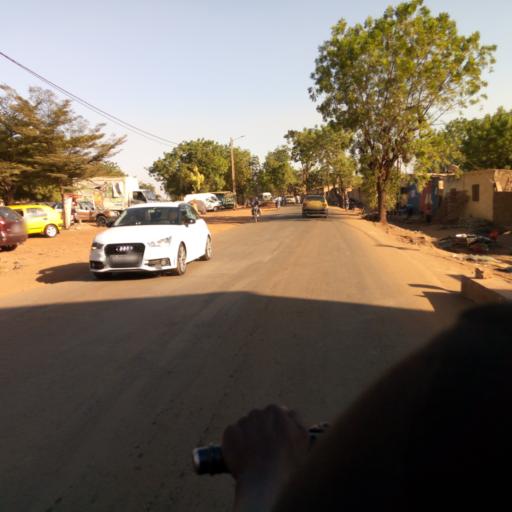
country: ML
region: Bamako
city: Bamako
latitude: 12.6583
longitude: -8.0314
